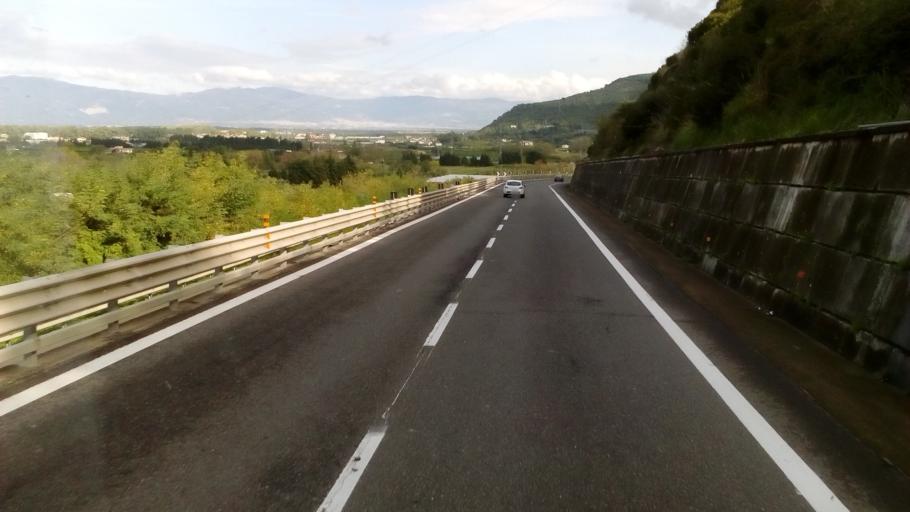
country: IT
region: Calabria
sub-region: Provincia di Vibo-Valentia
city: Pizzo
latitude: 38.7668
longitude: 16.2063
